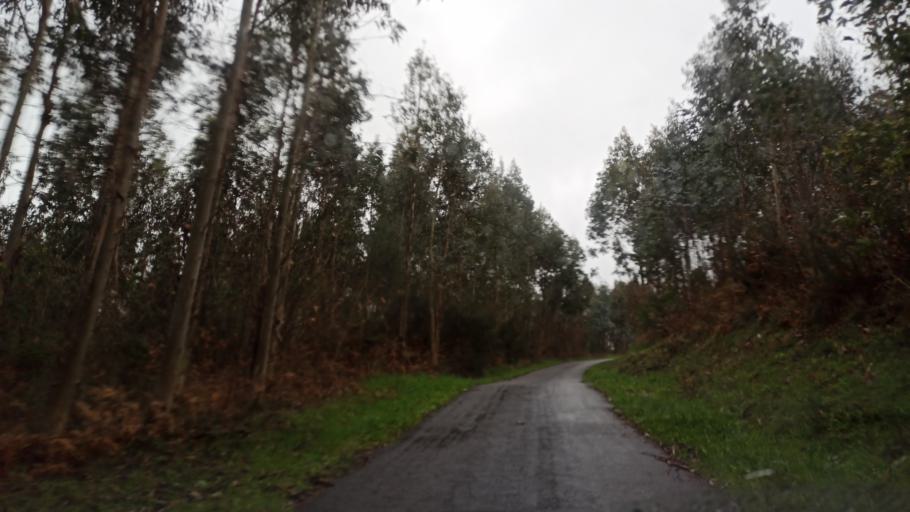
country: ES
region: Galicia
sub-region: Provincia da Coruna
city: Cesuras
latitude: 43.1784
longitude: -8.1569
